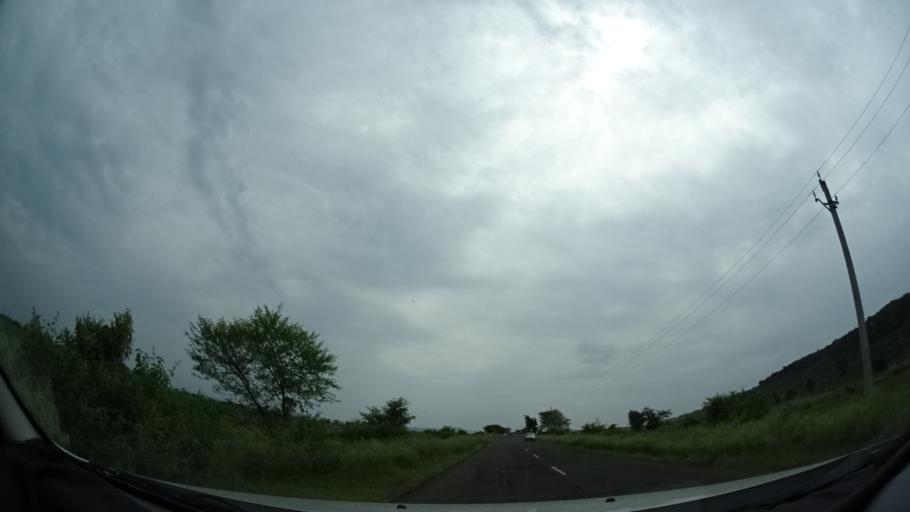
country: IN
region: Madhya Pradesh
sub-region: Raisen
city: Sultanpur
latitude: 23.3072
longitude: 78.0171
